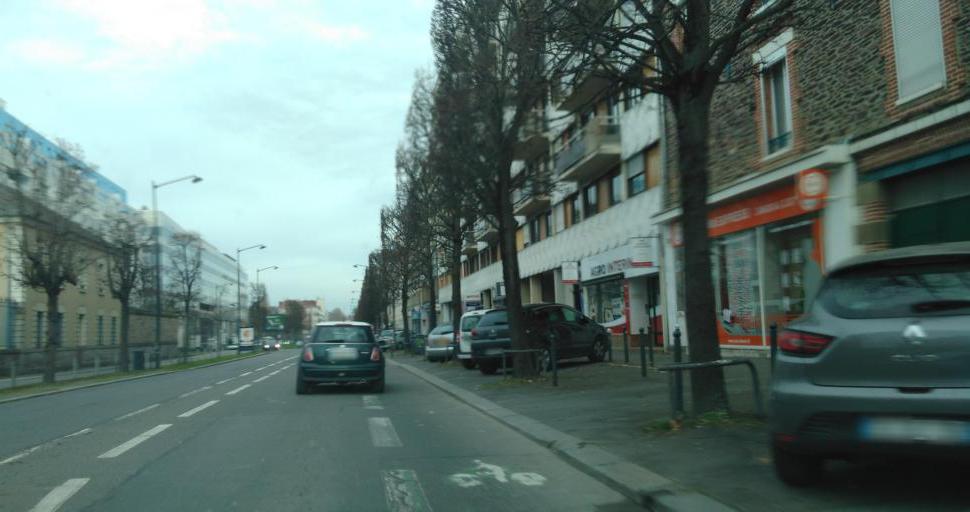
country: FR
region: Brittany
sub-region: Departement d'Ille-et-Vilaine
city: Rennes
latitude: 48.1027
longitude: -1.6843
